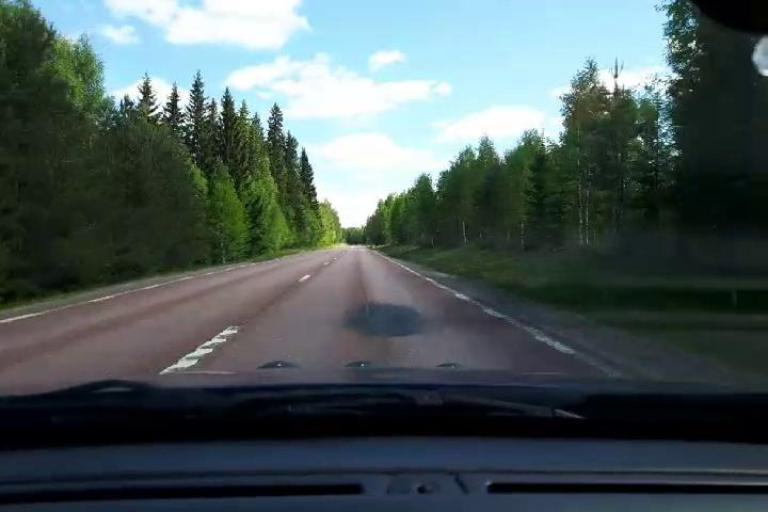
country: SE
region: Gaevleborg
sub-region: Ljusdals Kommun
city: Farila
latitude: 61.9275
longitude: 15.5686
